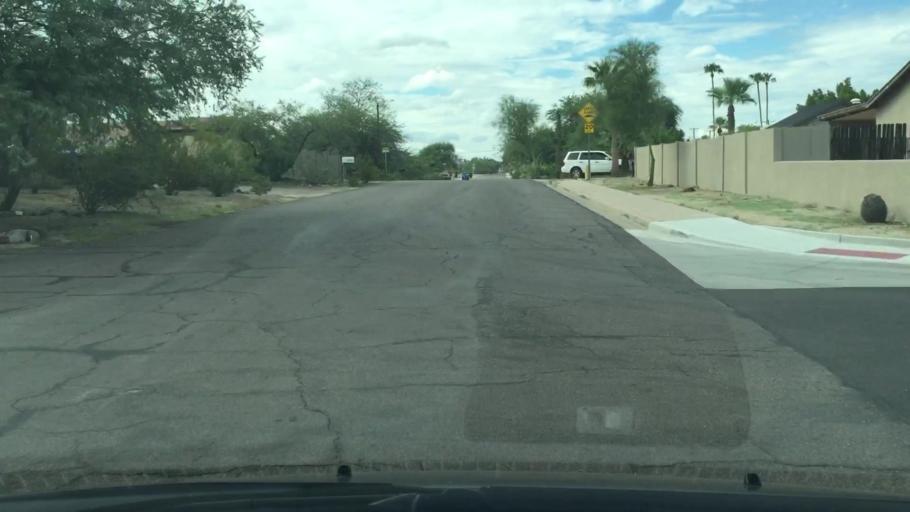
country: US
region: Arizona
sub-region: Maricopa County
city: Guadalupe
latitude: 33.3669
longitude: -112.0458
